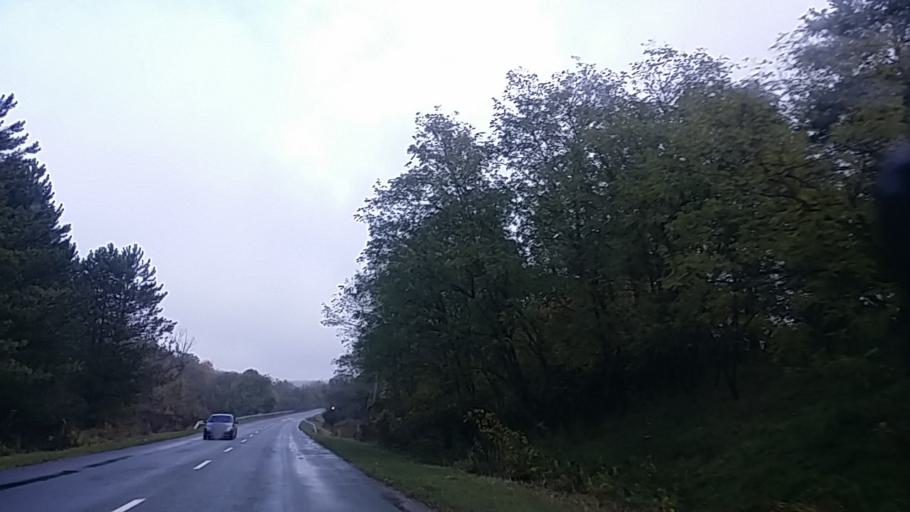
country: HU
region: Heves
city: Belapatfalva
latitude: 48.0731
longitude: 20.3584
